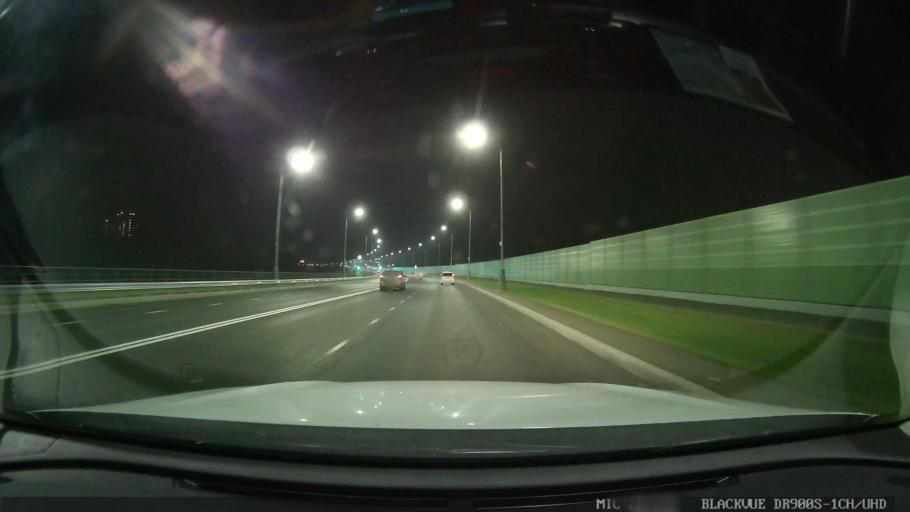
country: RU
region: Moskovskaya
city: Shcherbinka
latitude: 55.5080
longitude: 37.5464
